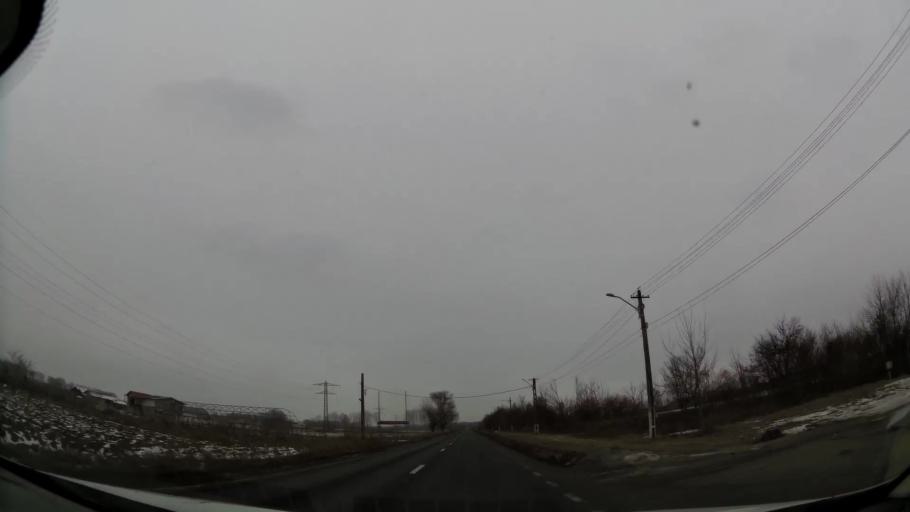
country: RO
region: Dambovita
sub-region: Comuna Contesti
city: Contesti
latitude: 44.6735
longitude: 25.6536
